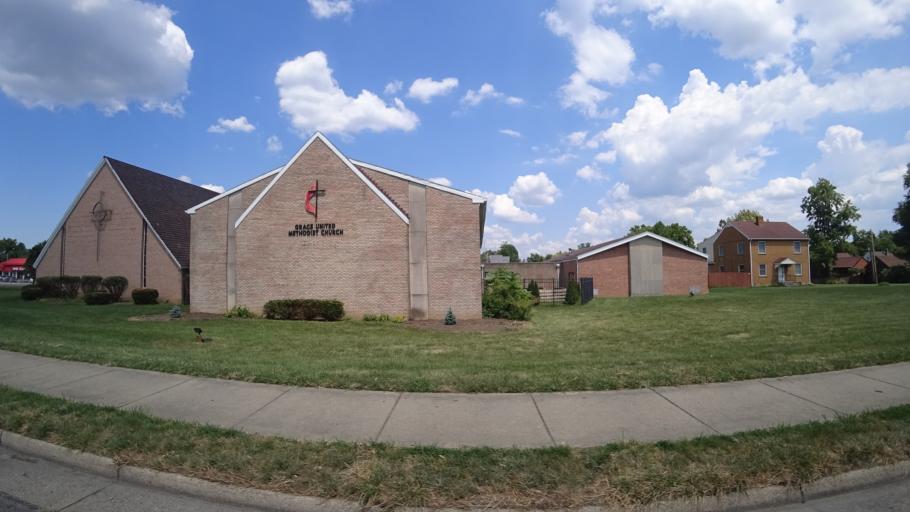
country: US
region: Ohio
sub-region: Butler County
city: Hamilton
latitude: 39.4165
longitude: -84.5852
